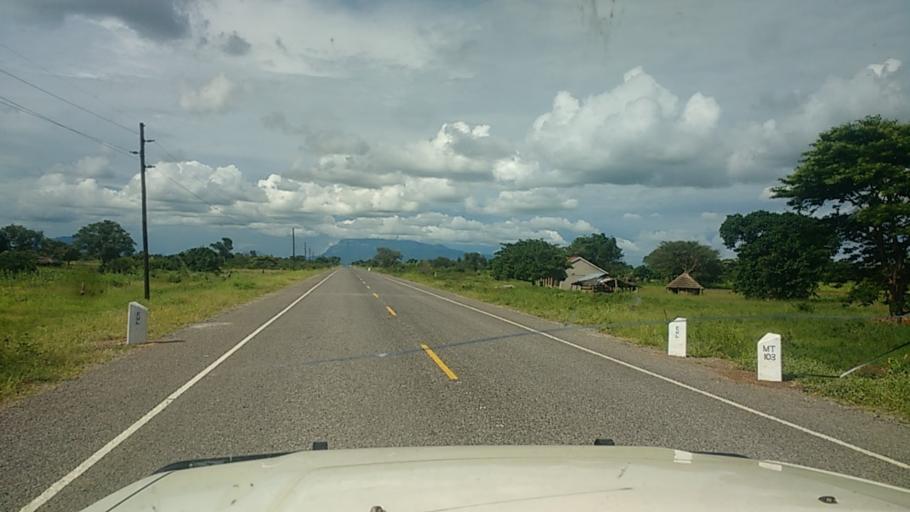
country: UG
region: Eastern Region
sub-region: Katakwi District
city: Katakwi
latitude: 1.9343
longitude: 34.0695
